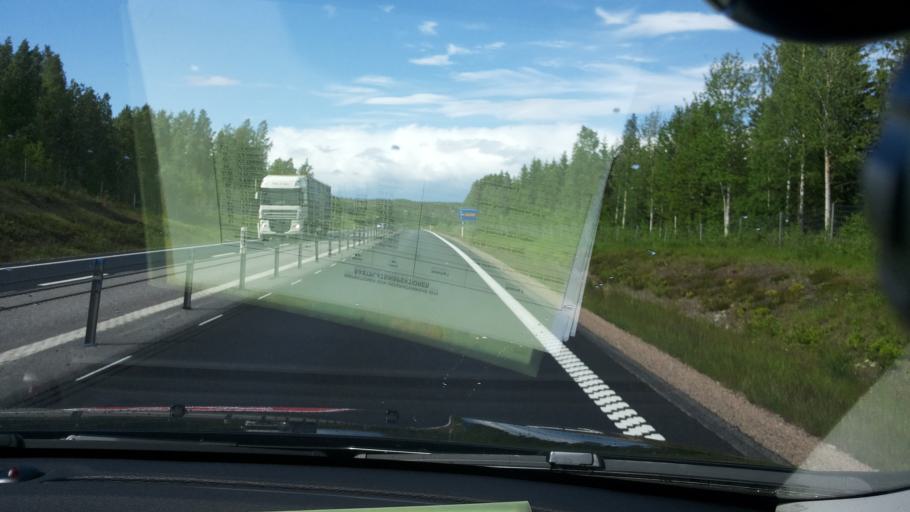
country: SE
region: Vaesternorrland
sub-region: Sundsvalls Kommun
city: Njurundabommen
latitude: 62.1792
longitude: 17.3571
